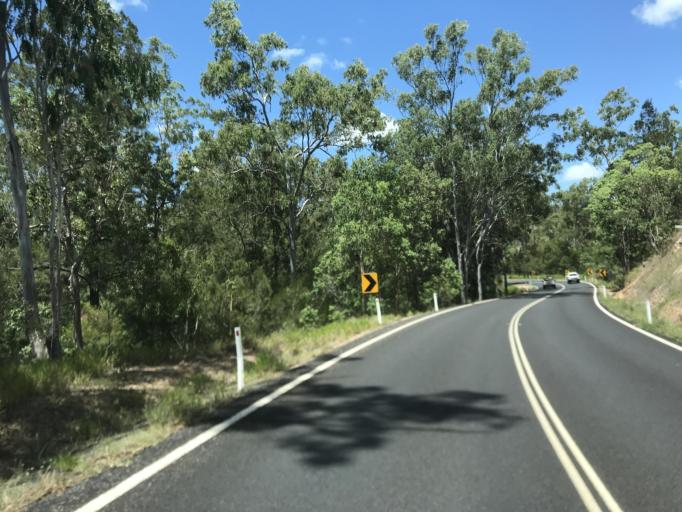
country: AU
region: Queensland
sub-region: Tablelands
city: Atherton
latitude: -17.4045
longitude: 145.3888
